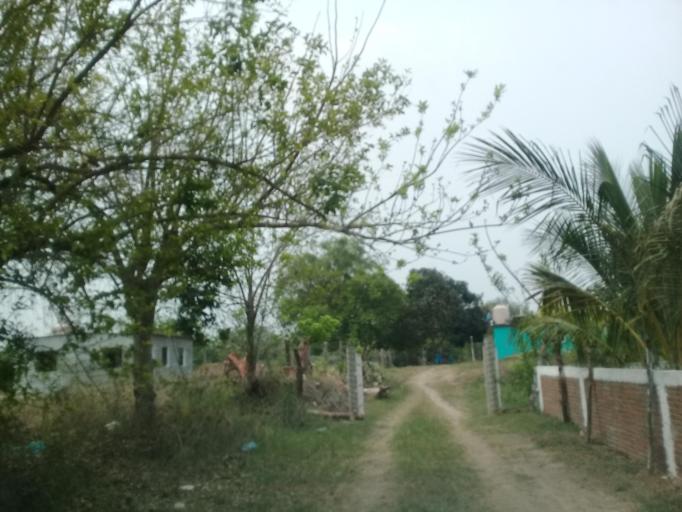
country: MX
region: Veracruz
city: Jamapa
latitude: 18.9549
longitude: -96.2037
